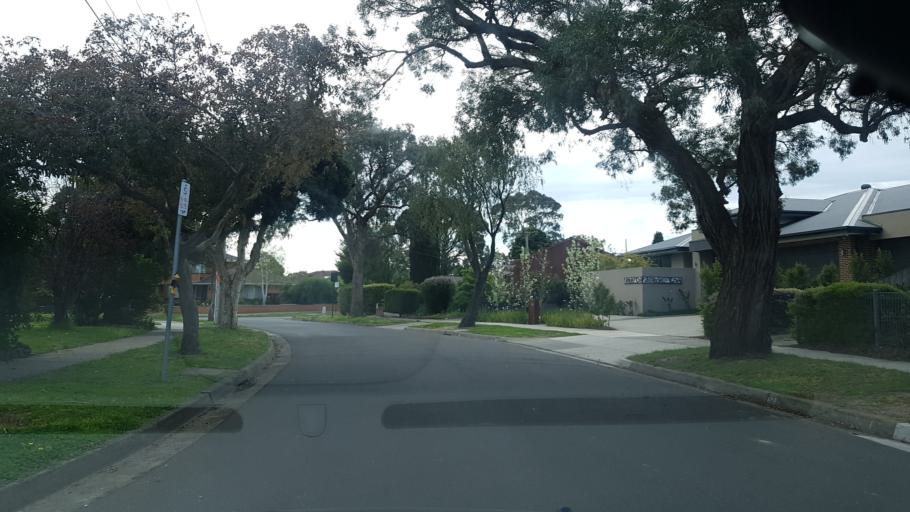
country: AU
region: Victoria
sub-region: Monash
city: Mulgrave
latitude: -37.9151
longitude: 145.1741
